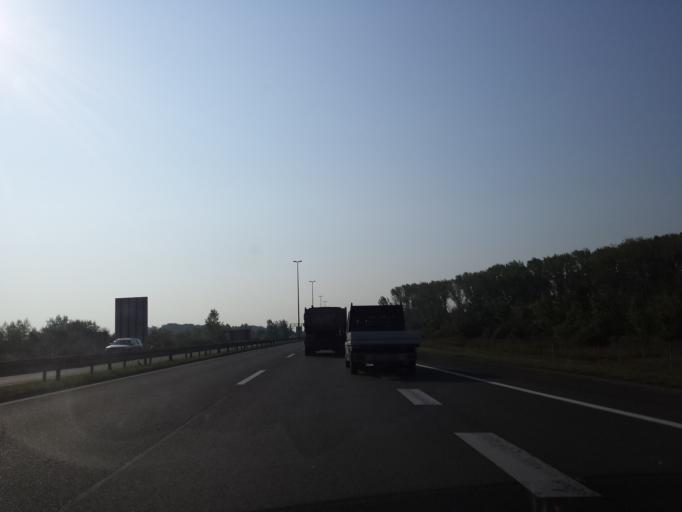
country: HR
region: Grad Zagreb
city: Jezdovec
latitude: 45.7849
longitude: 15.8596
